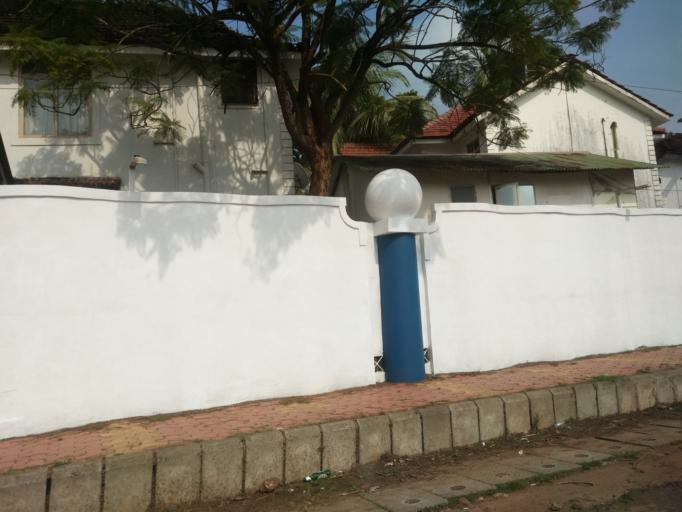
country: IN
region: Goa
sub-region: North Goa
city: Serula
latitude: 15.5363
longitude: 73.8202
